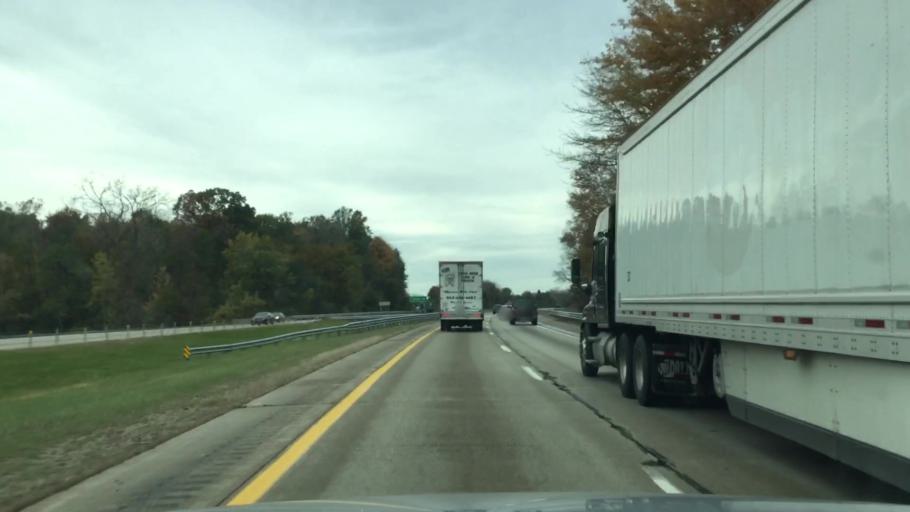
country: US
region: Michigan
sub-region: Calhoun County
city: Brownlee Park
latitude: 42.2877
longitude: -85.1190
